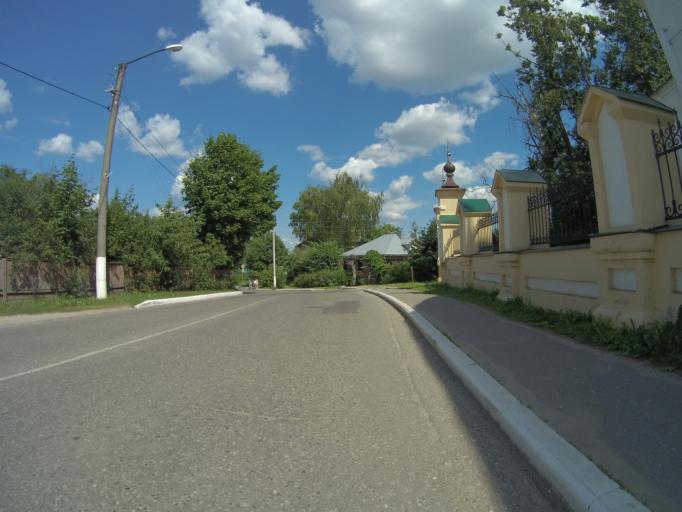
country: RU
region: Ivanovo
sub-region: Privolzhskiy Rayon
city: Ples
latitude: 57.4563
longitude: 41.5127
